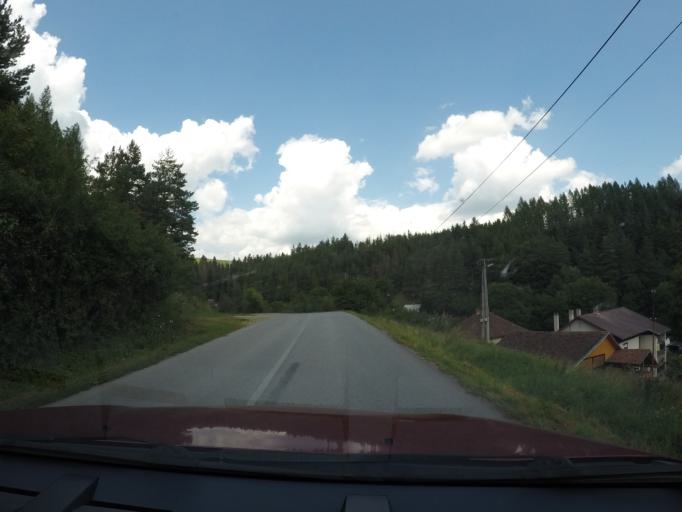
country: SK
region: Kosicky
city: Gelnica
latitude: 48.9132
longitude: 21.0857
